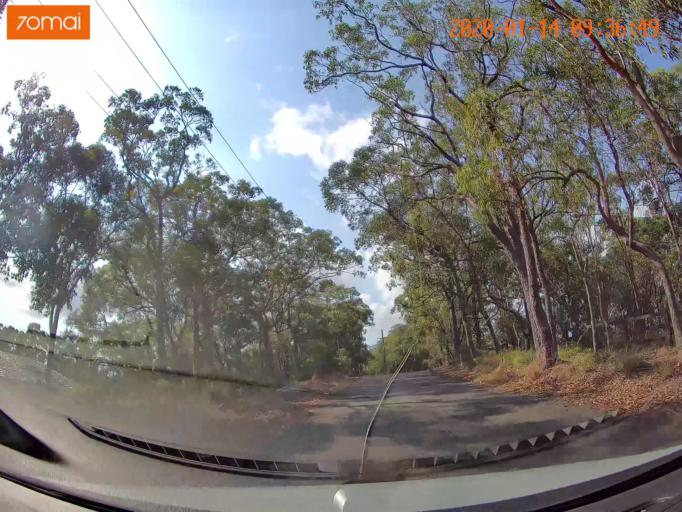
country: AU
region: New South Wales
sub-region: Wyong Shire
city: Kingfisher Shores
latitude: -33.1136
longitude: 151.5578
